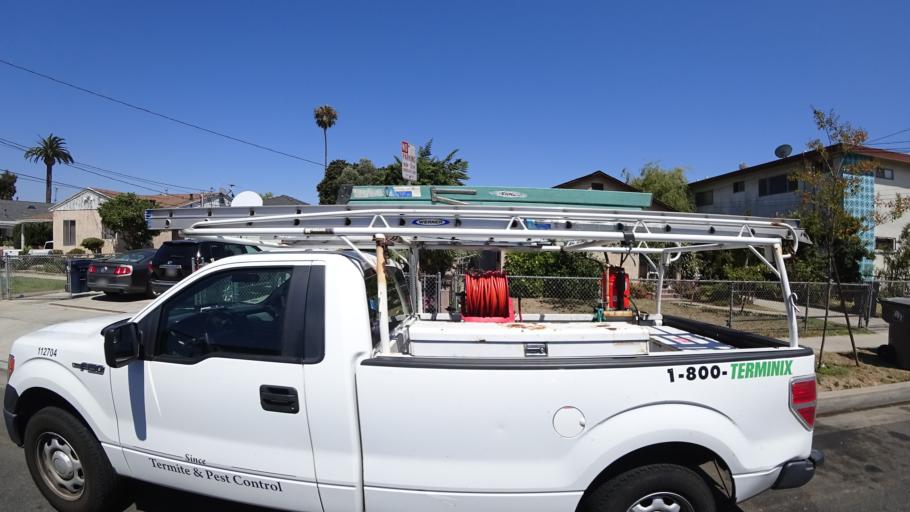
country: US
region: California
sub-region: Los Angeles County
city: Lennox
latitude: 33.9356
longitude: -118.3514
